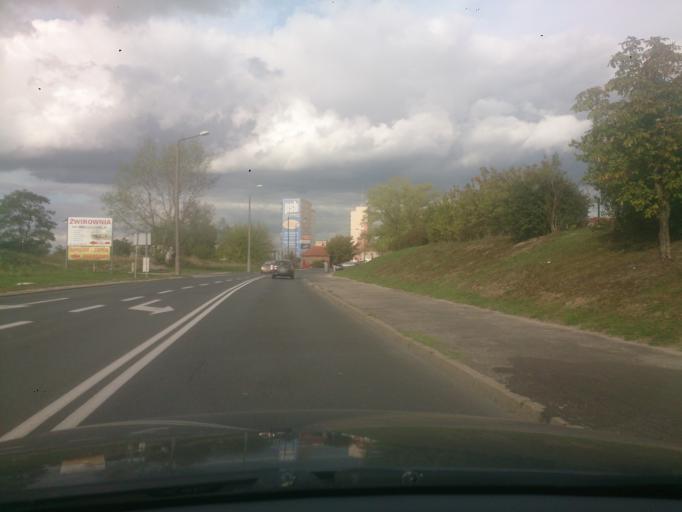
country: PL
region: Kujawsko-Pomorskie
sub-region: Grudziadz
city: Grudziadz
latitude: 53.4719
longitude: 18.7379
